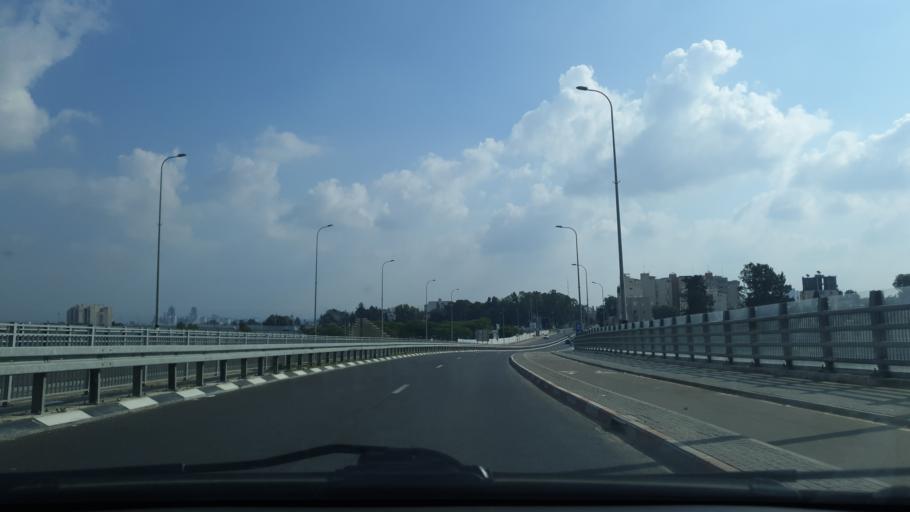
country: IL
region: Central District
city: Ramla
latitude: 31.9420
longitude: 34.8647
